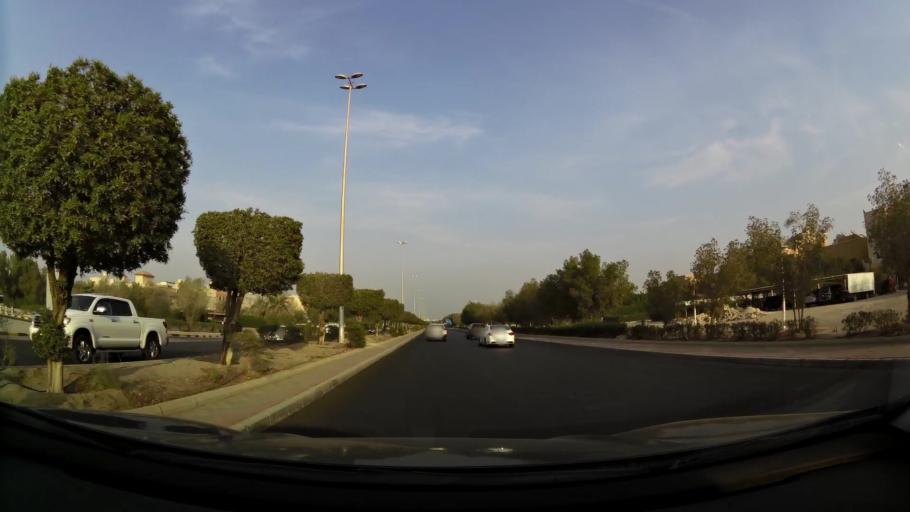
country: KW
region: Mubarak al Kabir
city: Sabah as Salim
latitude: 29.2418
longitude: 48.0640
